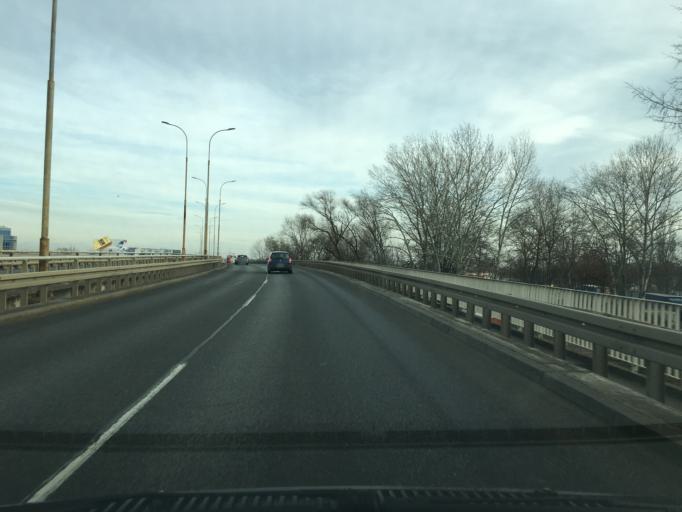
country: PL
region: Lower Silesian Voivodeship
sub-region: Powiat wroclawski
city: Wilczyce
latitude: 51.1510
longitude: 17.1244
